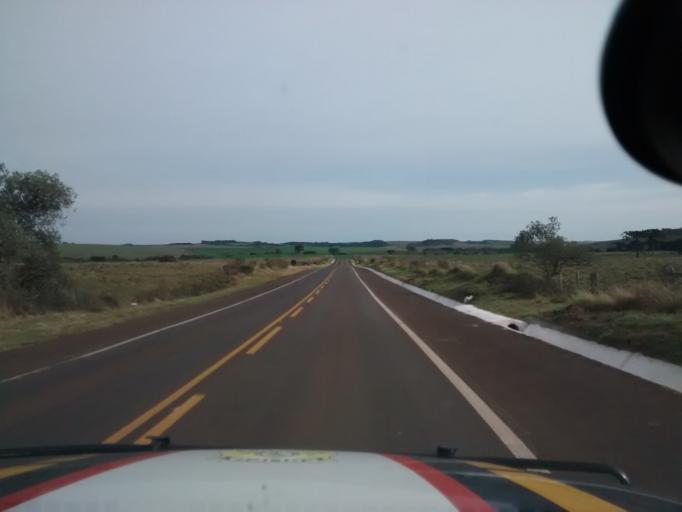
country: BR
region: Rio Grande do Sul
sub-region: Lagoa Vermelha
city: Lagoa Vermelha
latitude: -28.3289
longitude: -51.3237
